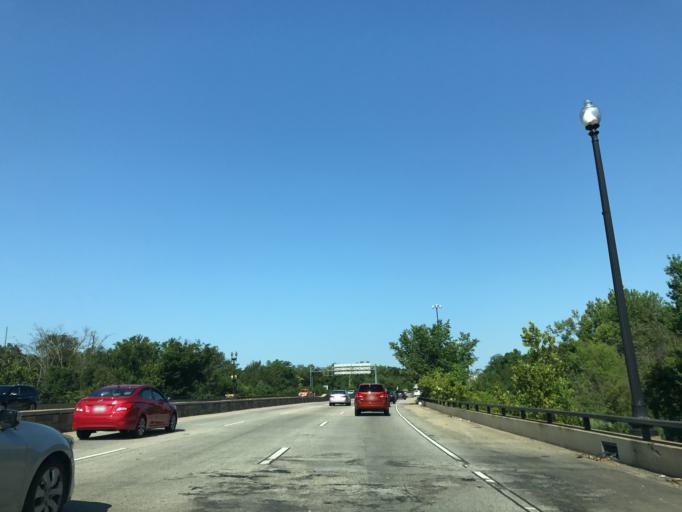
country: US
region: Maryland
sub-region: Prince George's County
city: Colmar Manor
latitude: 38.9180
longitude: -76.9424
